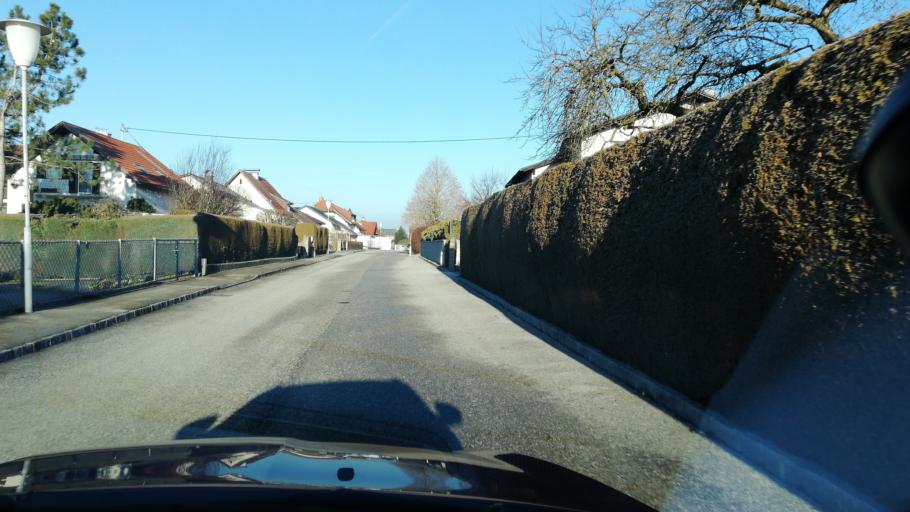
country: AT
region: Upper Austria
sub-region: Politischer Bezirk Steyr-Land
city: Bad Hall
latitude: 48.0345
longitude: 14.2161
